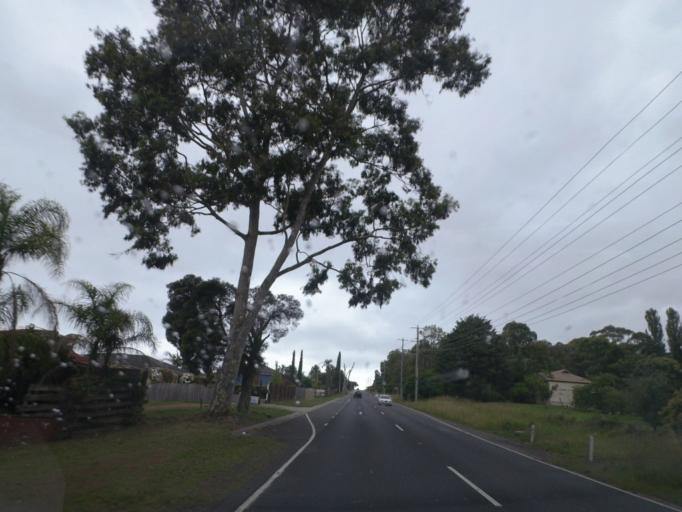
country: AU
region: Victoria
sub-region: Yarra Ranges
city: Mount Evelyn
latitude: -37.7822
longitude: 145.4203
